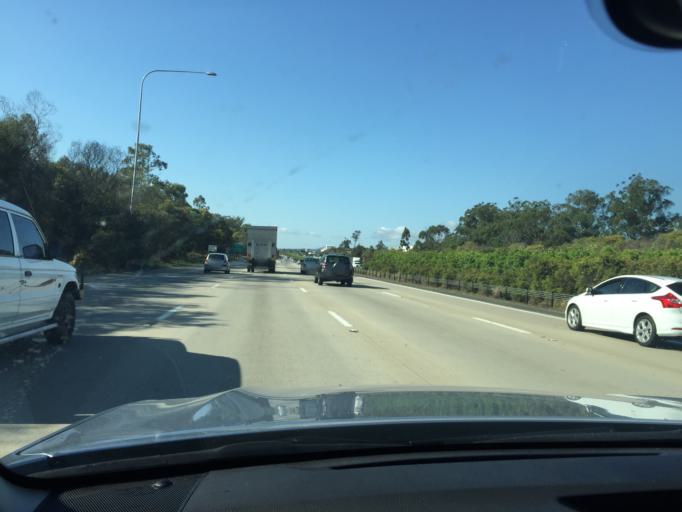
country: AU
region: Queensland
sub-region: Gold Coast
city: Yatala
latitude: -27.7415
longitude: 153.2320
